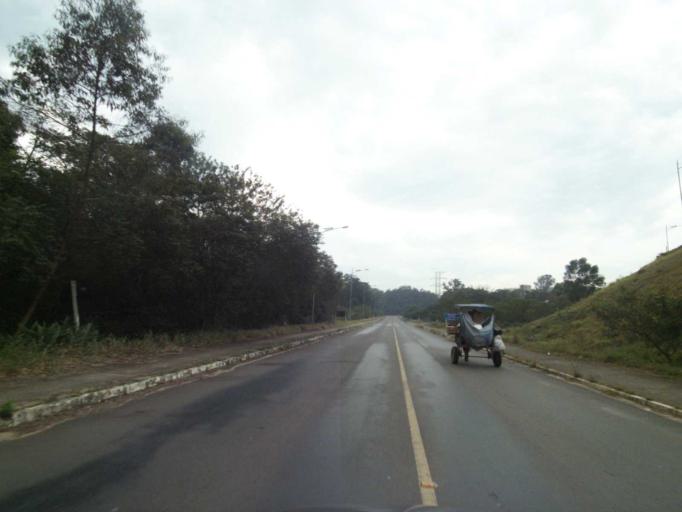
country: BR
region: Rio Grande do Sul
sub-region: Sao Leopoldo
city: Sao Leopoldo
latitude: -29.7881
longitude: -51.1654
